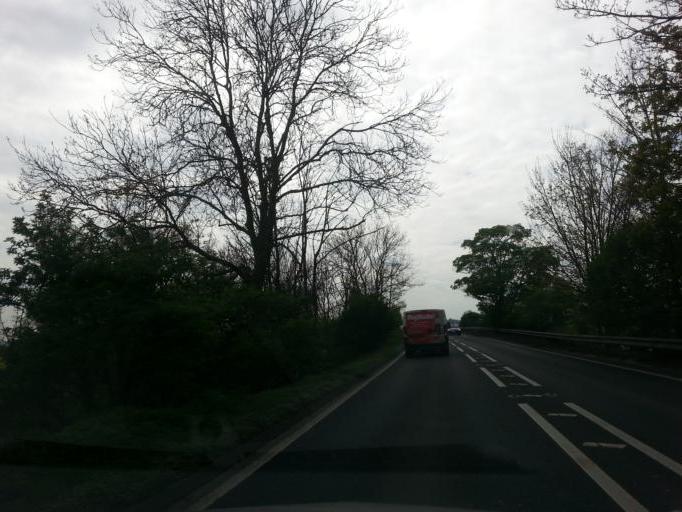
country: GB
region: England
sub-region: Cambridgeshire
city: March
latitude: 52.6234
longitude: 0.0877
